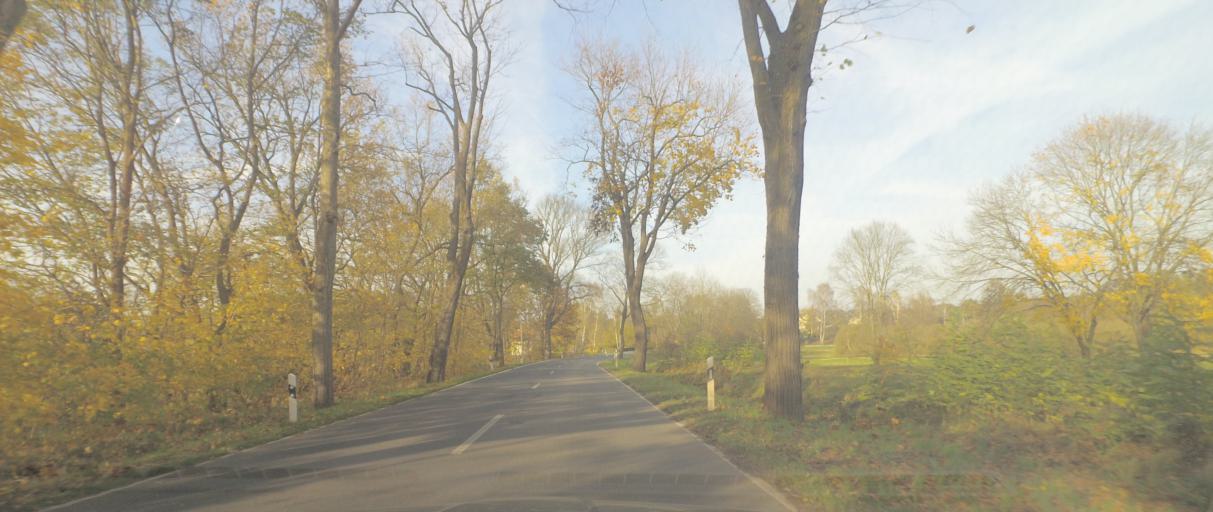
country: DE
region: Brandenburg
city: Zossen
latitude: 52.1435
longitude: 13.4801
